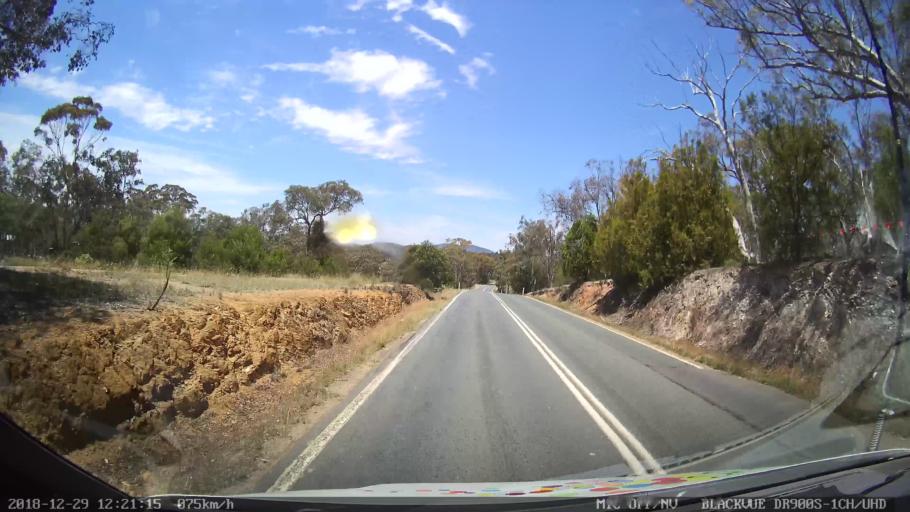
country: AU
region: New South Wales
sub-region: Queanbeyan
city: Queanbeyan
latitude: -35.4116
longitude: 149.2245
